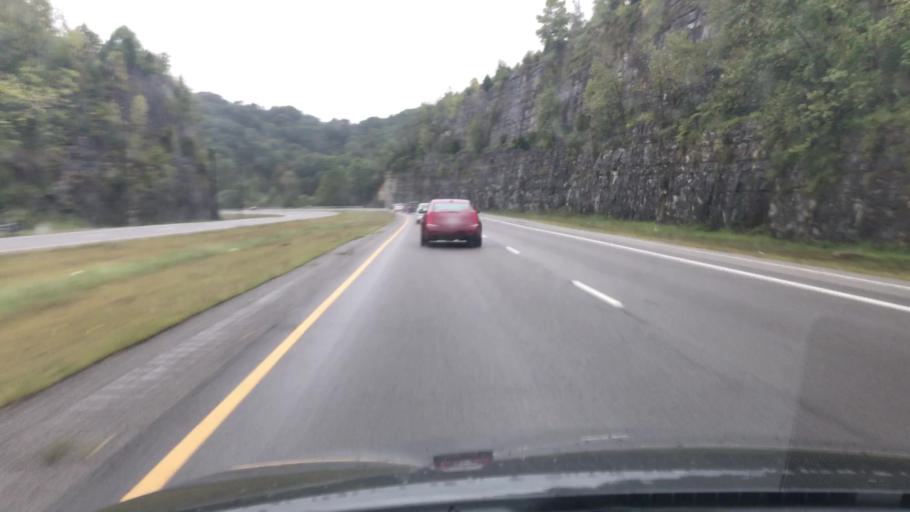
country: US
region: Tennessee
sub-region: Cheatham County
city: Ashland City
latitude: 36.2196
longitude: -86.9659
